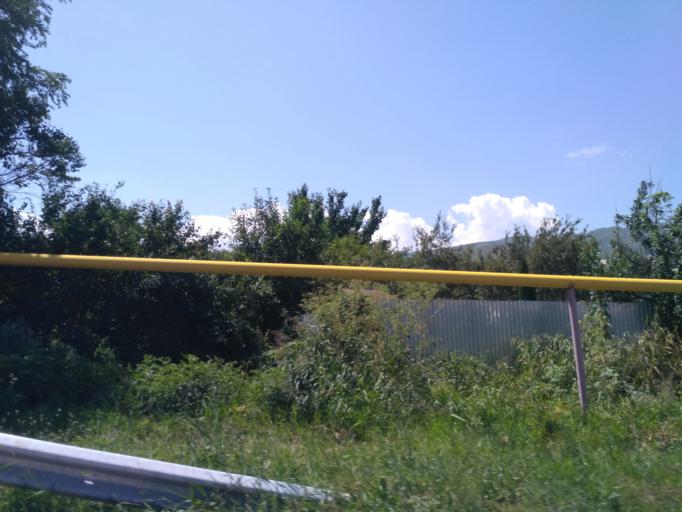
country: KZ
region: Almaty Oblysy
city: Burunday
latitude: 43.1657
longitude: 76.6063
